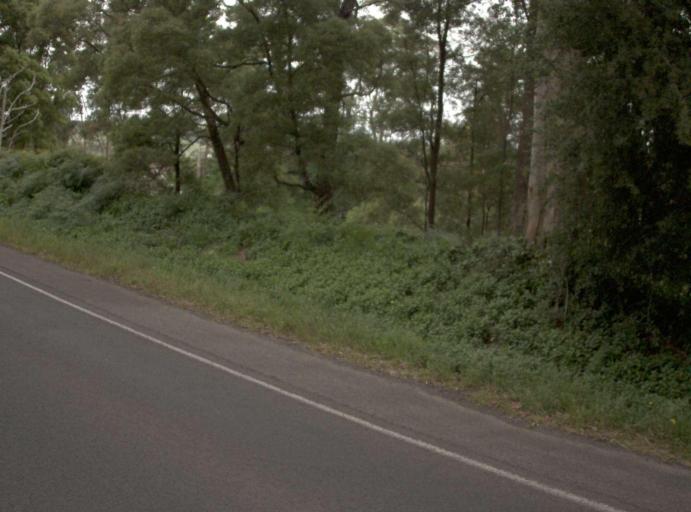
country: AU
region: Victoria
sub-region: Cardinia
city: Koo-Wee-Rup
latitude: -38.3665
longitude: 145.6647
